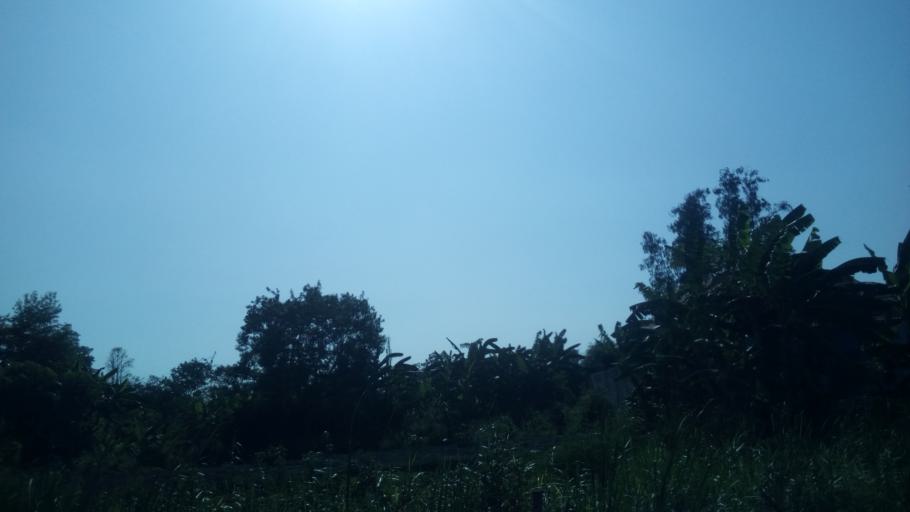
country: TH
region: Nakhon Pathom
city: Salaya
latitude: 13.8166
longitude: 100.3090
